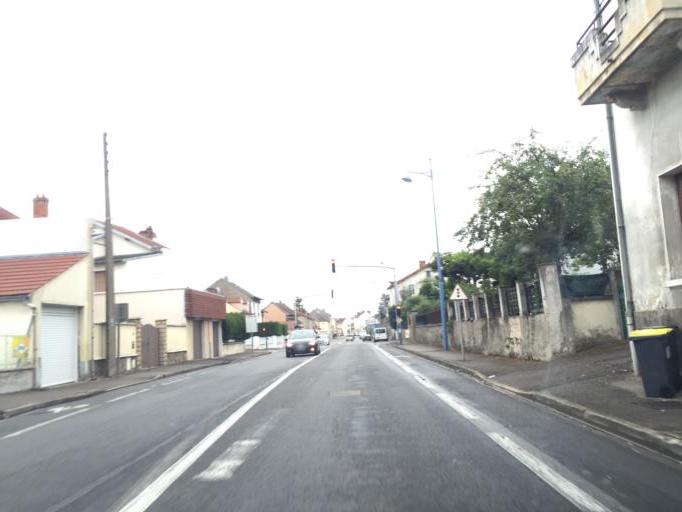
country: FR
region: Auvergne
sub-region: Departement de l'Allier
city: Bellerive-sur-Allier
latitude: 46.1204
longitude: 3.4060
